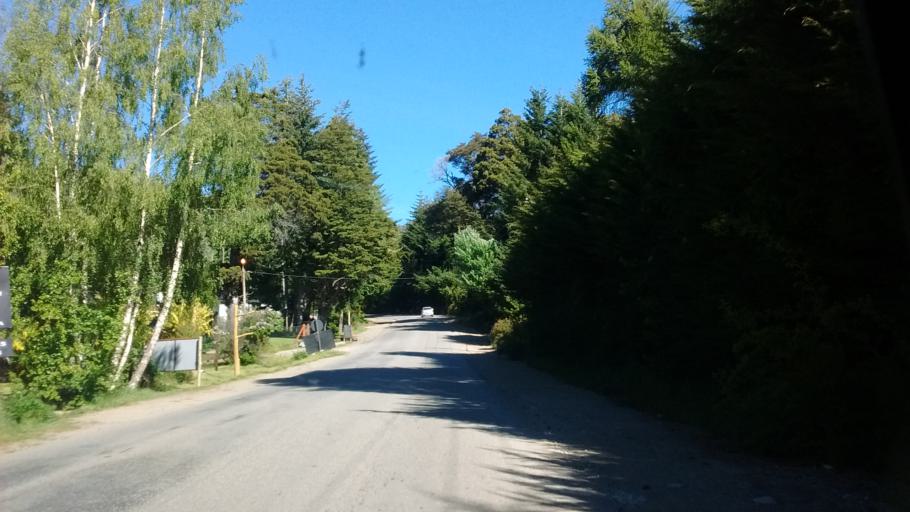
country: AR
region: Rio Negro
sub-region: Departamento de Bariloche
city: San Carlos de Bariloche
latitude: -41.0743
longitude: -71.5319
